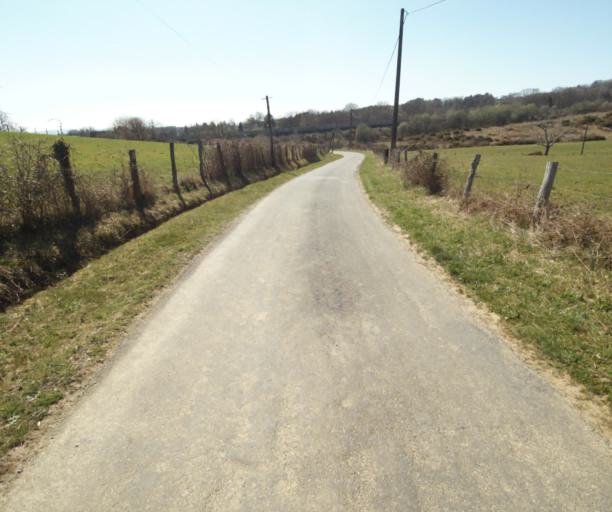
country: FR
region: Limousin
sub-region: Departement de la Correze
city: Saint-Clement
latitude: 45.3116
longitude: 1.6983
